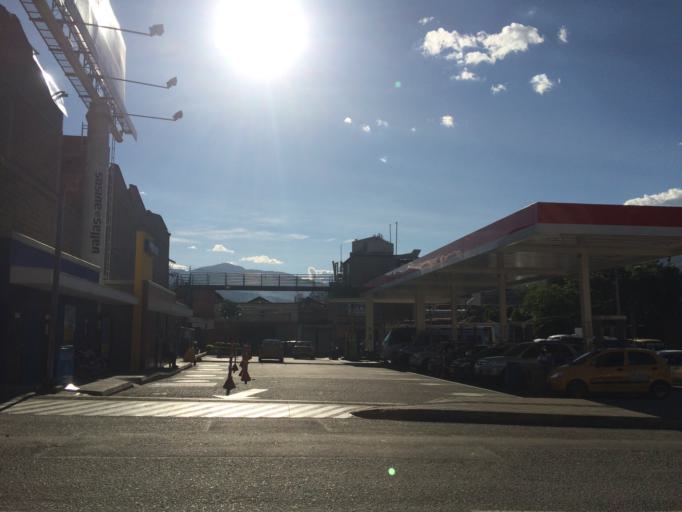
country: CO
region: Antioquia
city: Medellin
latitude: 6.2408
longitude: -75.5698
